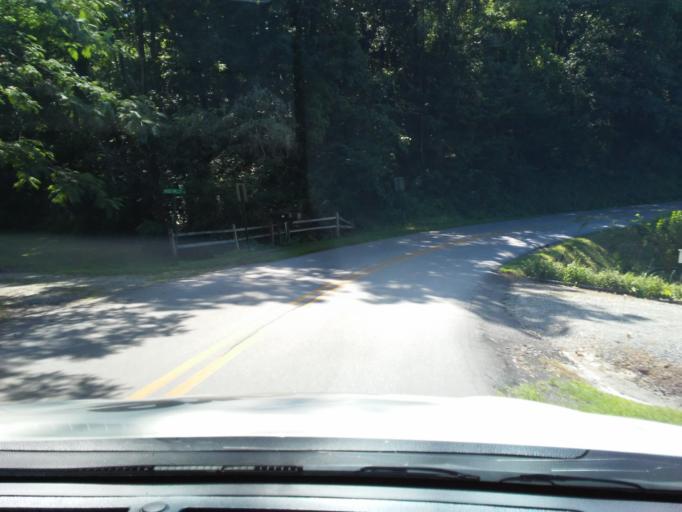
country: US
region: Georgia
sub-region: Union County
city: Blairsville
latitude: 34.9249
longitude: -83.8655
